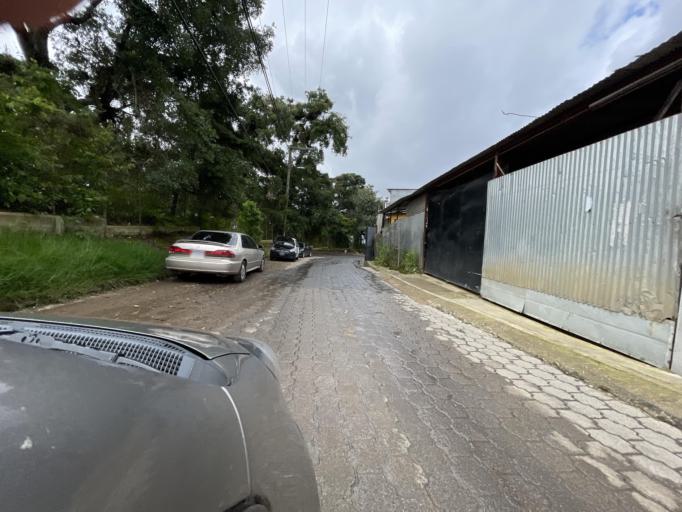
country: GT
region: Guatemala
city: Mixco
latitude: 14.6393
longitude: -90.6215
